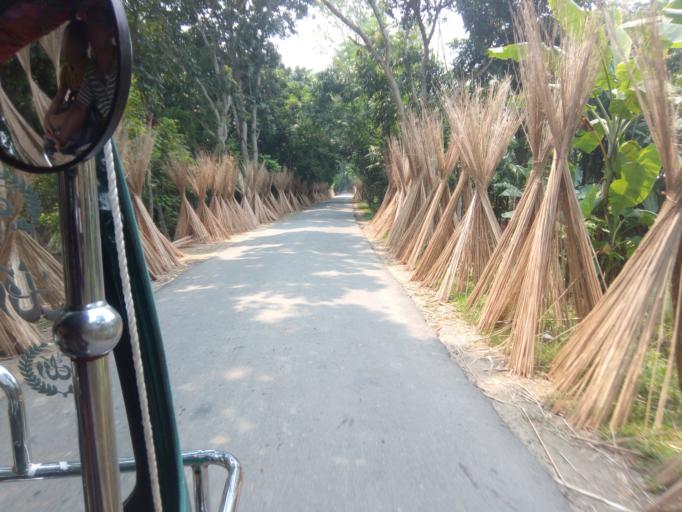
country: BD
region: Khulna
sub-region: Magura
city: Magura
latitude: 23.5032
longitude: 89.6117
